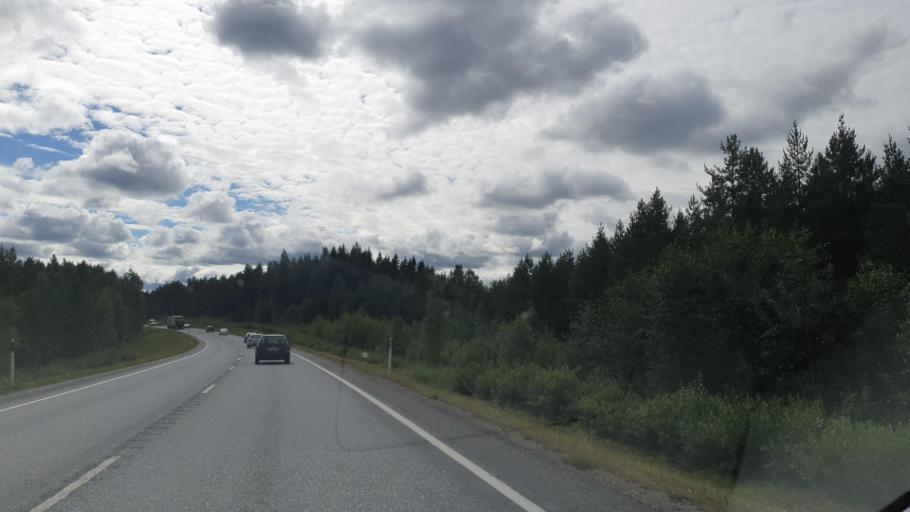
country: FI
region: Kainuu
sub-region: Kajaani
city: Kajaani
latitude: 64.1670
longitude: 27.5303
